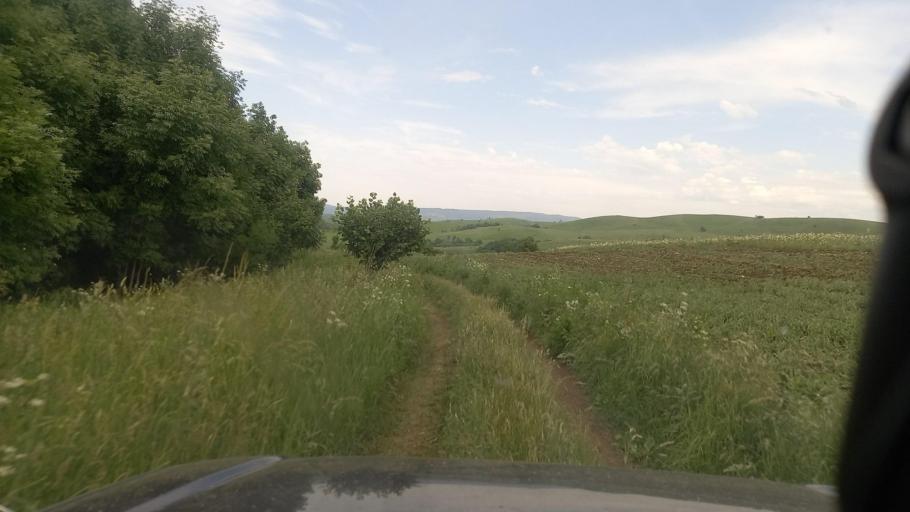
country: RU
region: Krasnodarskiy
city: Peredovaya
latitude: 44.0793
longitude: 41.3479
